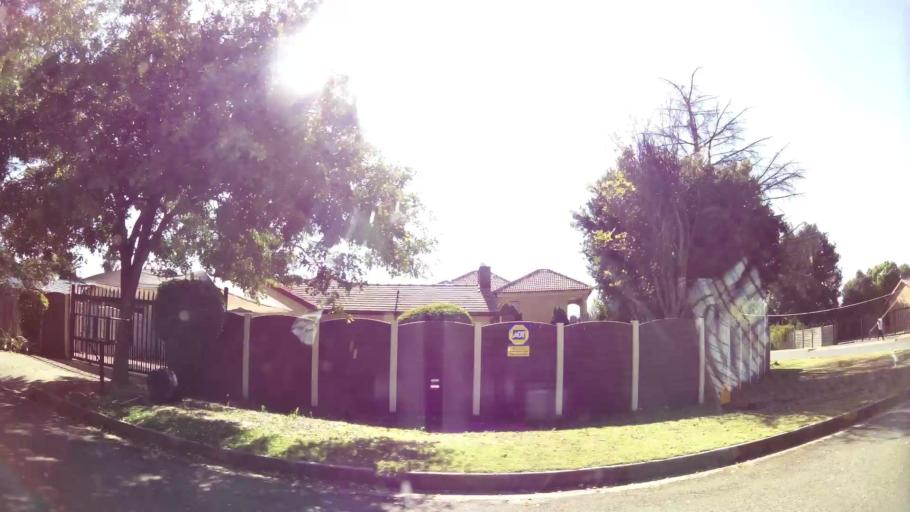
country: ZA
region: Gauteng
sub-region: City of Johannesburg Metropolitan Municipality
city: Modderfontein
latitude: -26.0616
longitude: 28.2086
